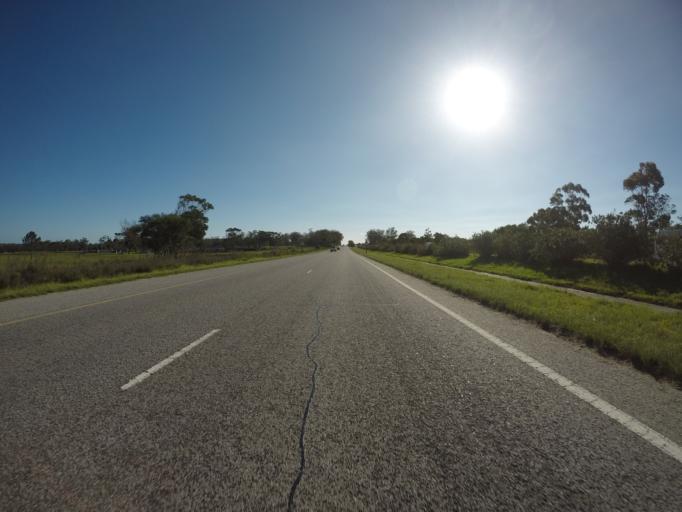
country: ZA
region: Eastern Cape
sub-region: Nelson Mandela Bay Metropolitan Municipality
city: Uitenhage
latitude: -33.9375
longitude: 25.3707
